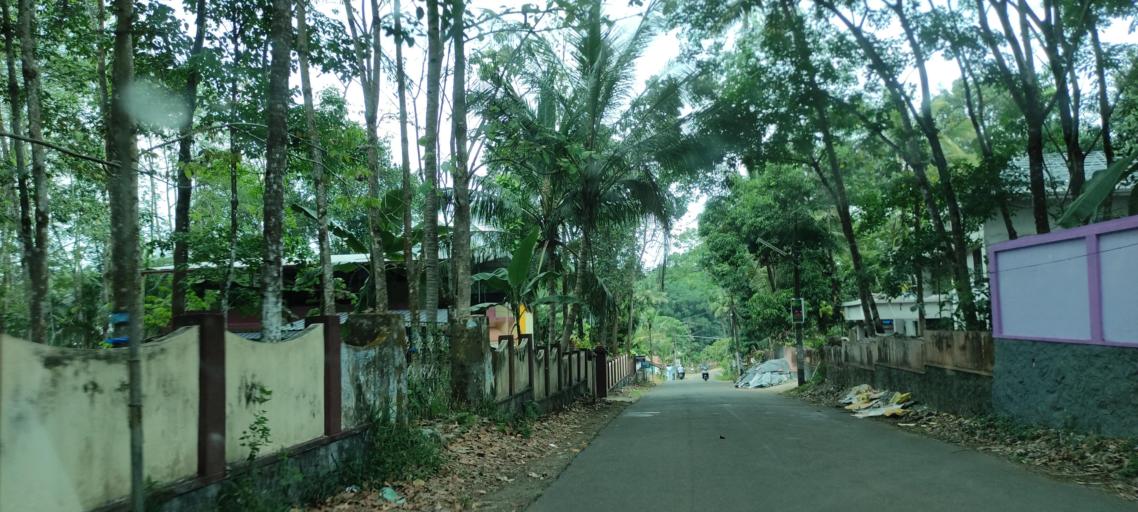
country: IN
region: Kerala
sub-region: Pattanamtitta
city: Adur
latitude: 9.1678
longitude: 76.7359
